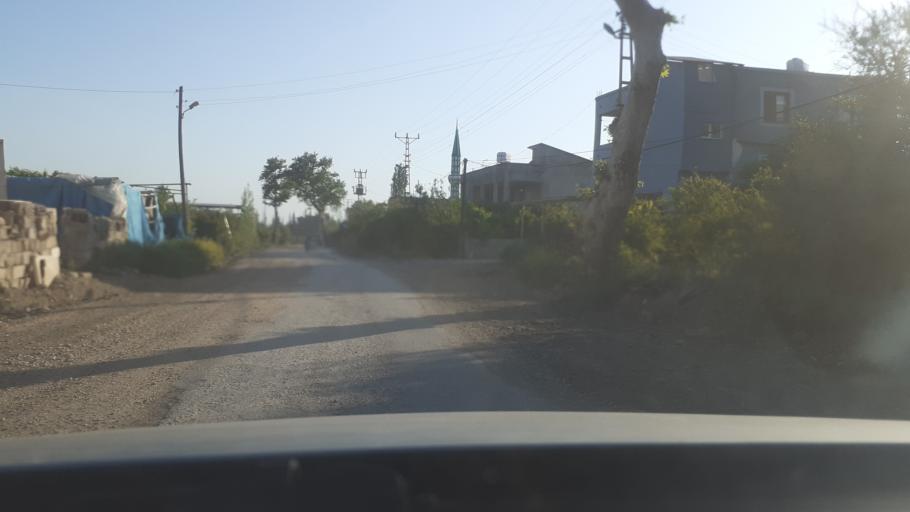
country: TR
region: Hatay
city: Kirikhan
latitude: 36.4769
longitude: 36.3186
